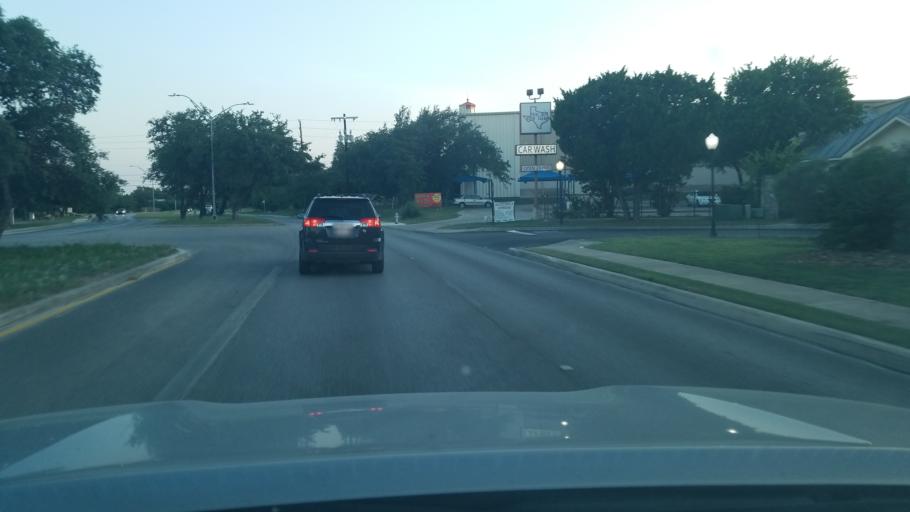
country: US
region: Texas
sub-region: Bexar County
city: Shavano Park
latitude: 29.5811
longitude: -98.5397
